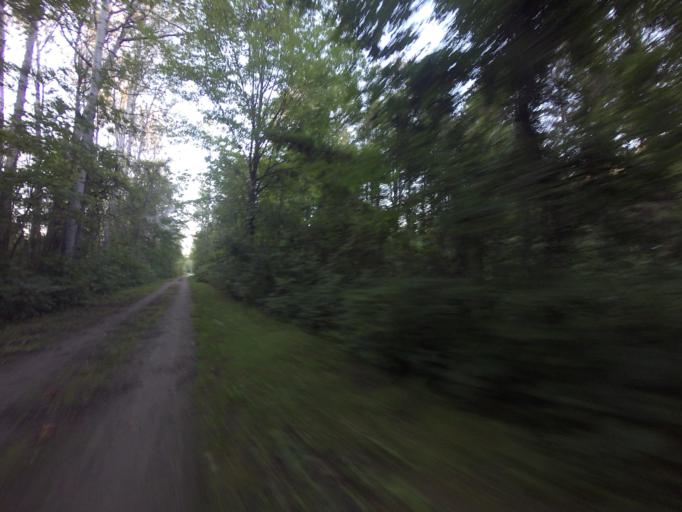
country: CA
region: Ontario
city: Brampton
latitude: 43.9176
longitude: -79.8411
